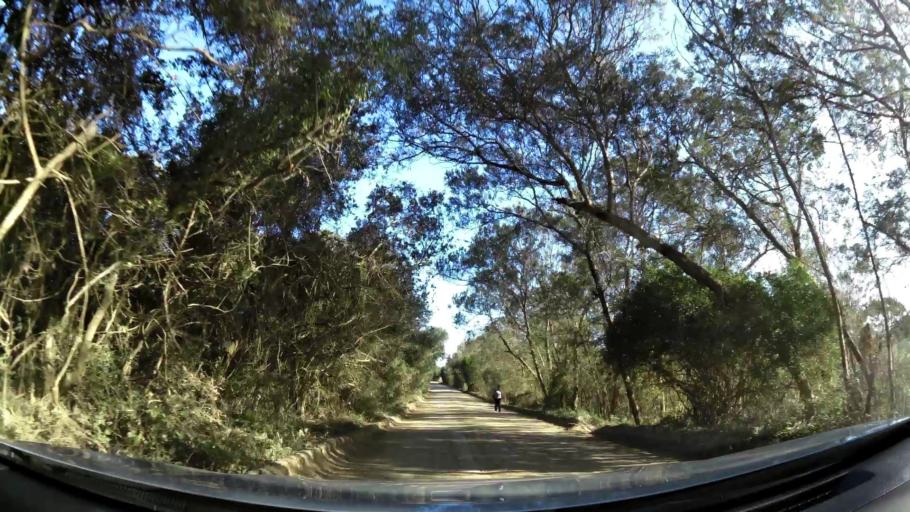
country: ZA
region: Western Cape
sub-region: Eden District Municipality
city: George
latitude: -33.9866
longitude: 22.5677
